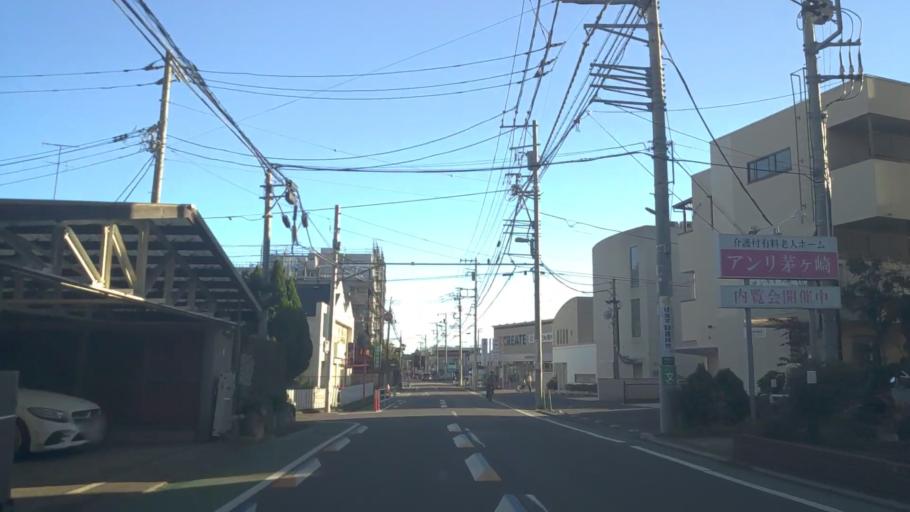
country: JP
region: Kanagawa
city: Chigasaki
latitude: 35.3308
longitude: 139.4146
